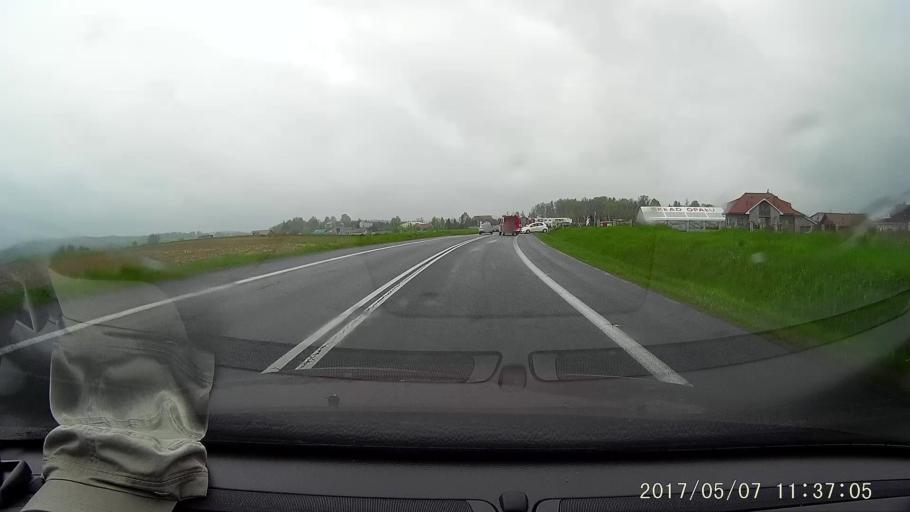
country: PL
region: Lower Silesian Voivodeship
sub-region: Powiat lubanski
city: Pisarzowice
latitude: 51.1357
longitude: 15.2465
